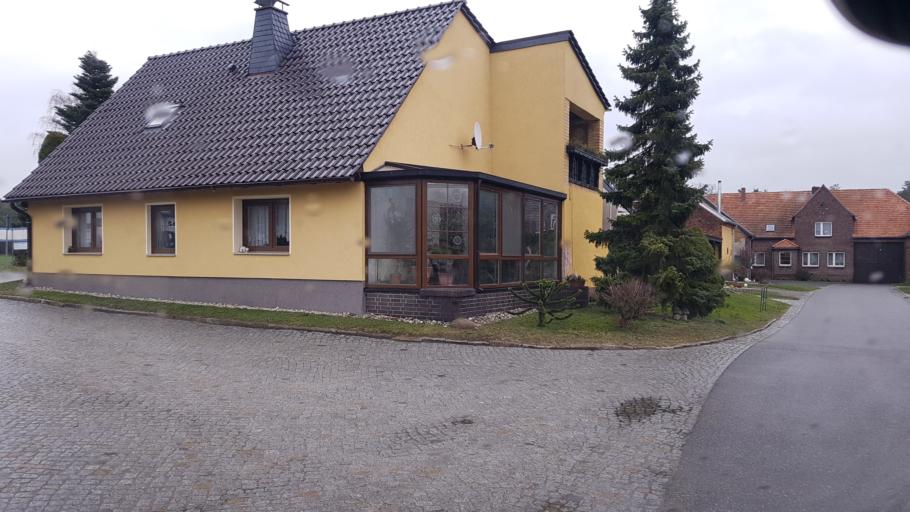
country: DE
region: Brandenburg
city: Sonnewalde
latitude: 51.6770
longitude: 13.6842
